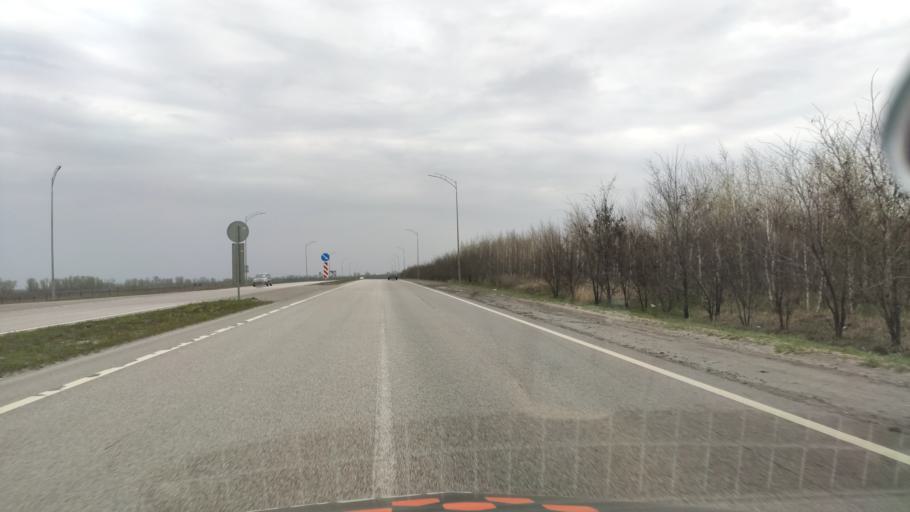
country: RU
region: Belgorod
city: Staryy Oskol
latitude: 51.3746
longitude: 37.8490
